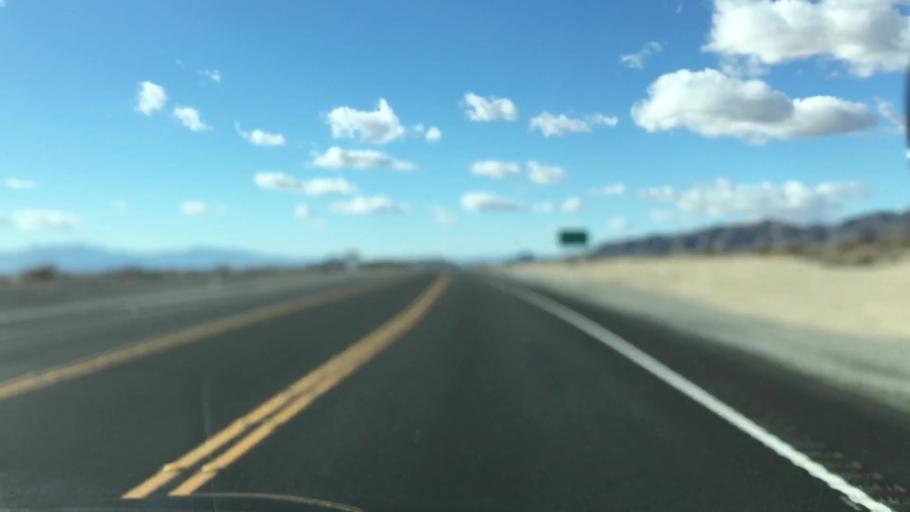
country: US
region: Nevada
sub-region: Nye County
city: Pahrump
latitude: 36.5643
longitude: -116.1196
